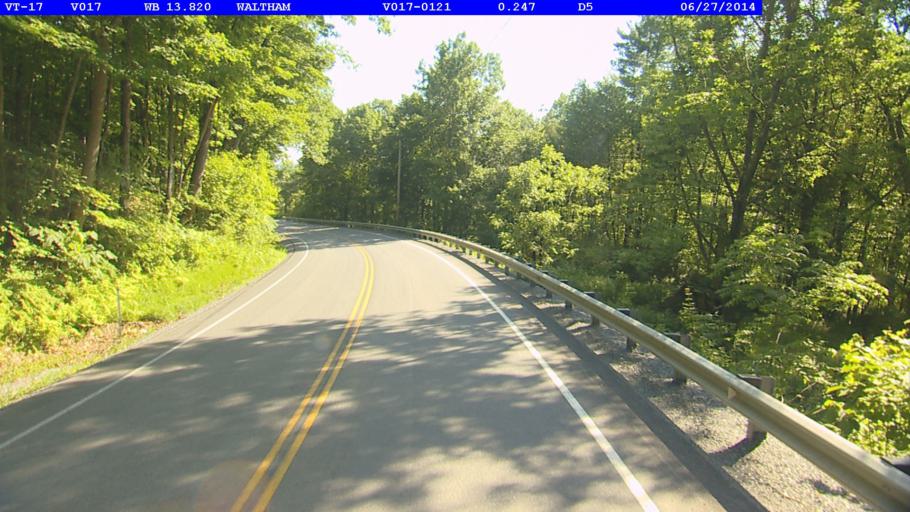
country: US
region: Vermont
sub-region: Addison County
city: Vergennes
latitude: 44.1122
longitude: -73.2178
